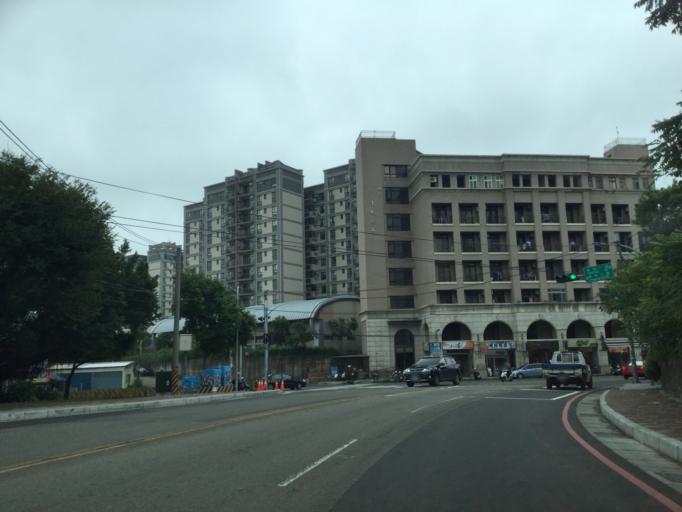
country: TW
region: Taiwan
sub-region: Hsinchu
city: Hsinchu
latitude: 24.7969
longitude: 121.0016
